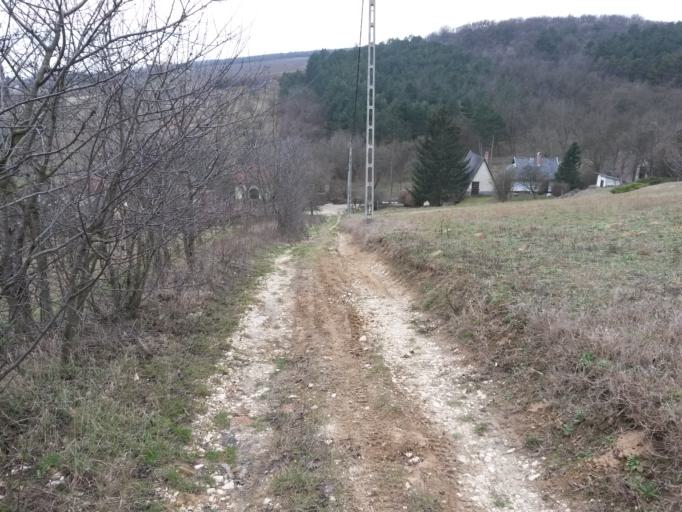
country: HU
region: Pest
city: Zsambek
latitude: 47.5744
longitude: 18.7264
